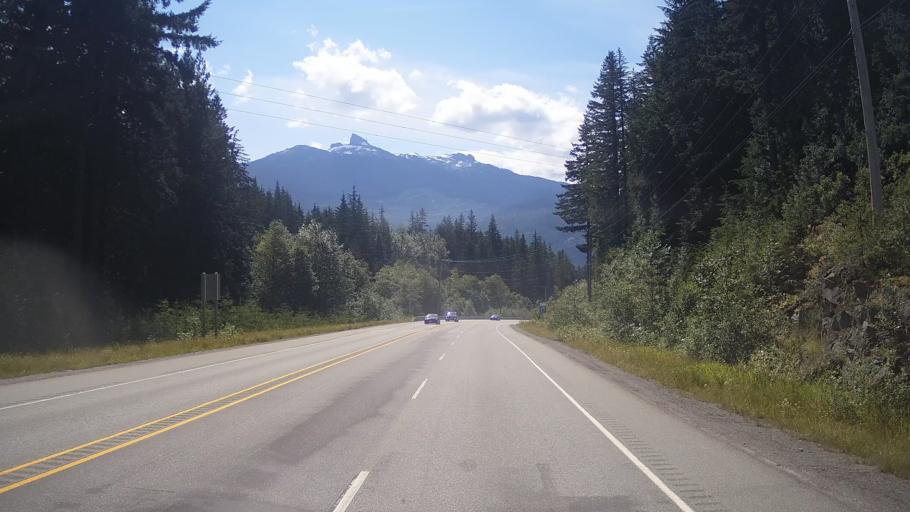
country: CA
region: British Columbia
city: Whistler
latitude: 50.0436
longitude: -123.1249
